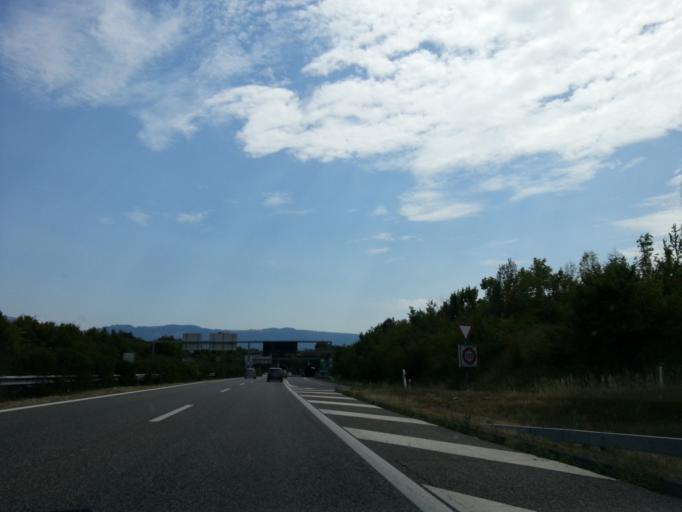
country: CH
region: Geneva
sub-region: Geneva
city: Bernex
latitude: 46.1871
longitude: 6.0813
